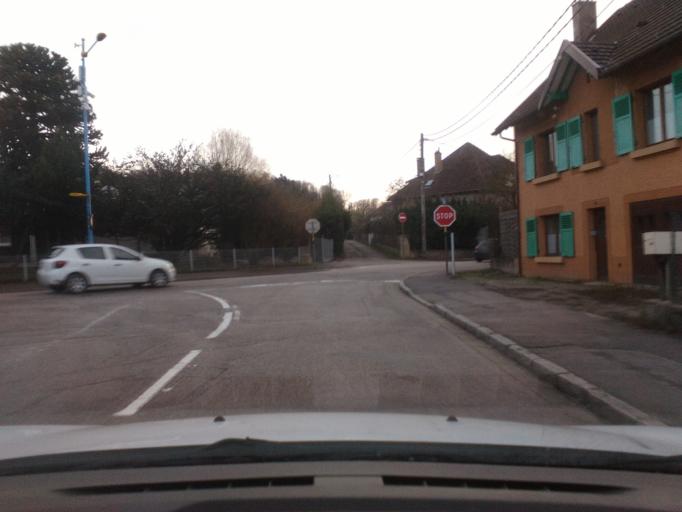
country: FR
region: Lorraine
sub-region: Departement des Vosges
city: Charmes
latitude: 48.3700
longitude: 6.2847
